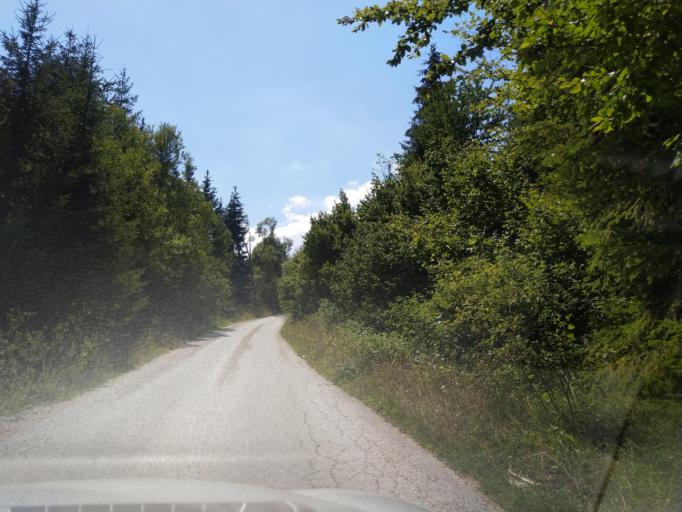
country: RS
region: Central Serbia
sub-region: Zlatiborski Okrug
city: Nova Varos
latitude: 43.4724
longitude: 19.9632
